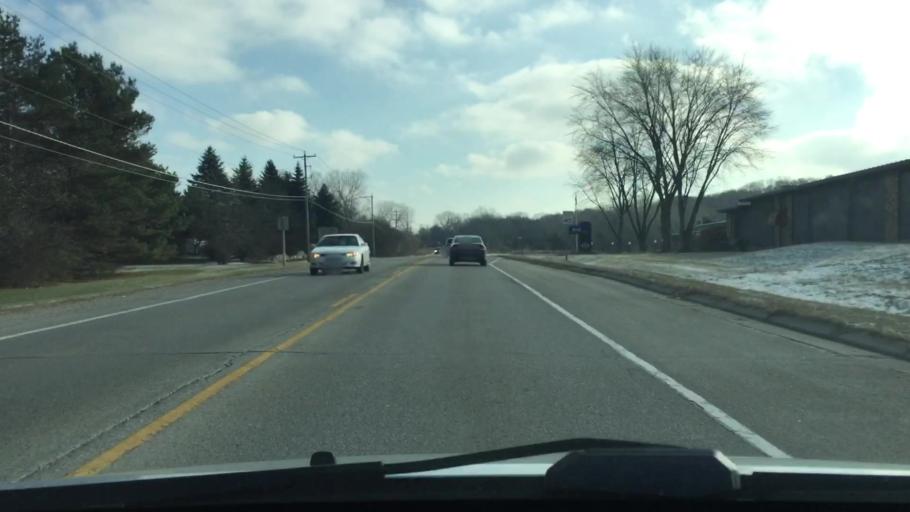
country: US
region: Wisconsin
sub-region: Waukesha County
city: Wales
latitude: 43.0120
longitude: -88.3953
